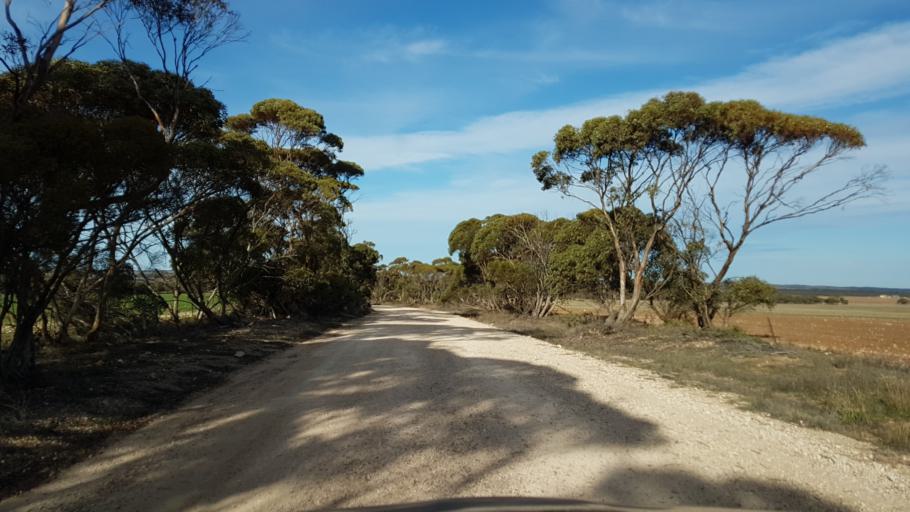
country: AU
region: South Australia
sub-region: Mid Murray
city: Mannum
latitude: -34.9788
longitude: 139.5754
